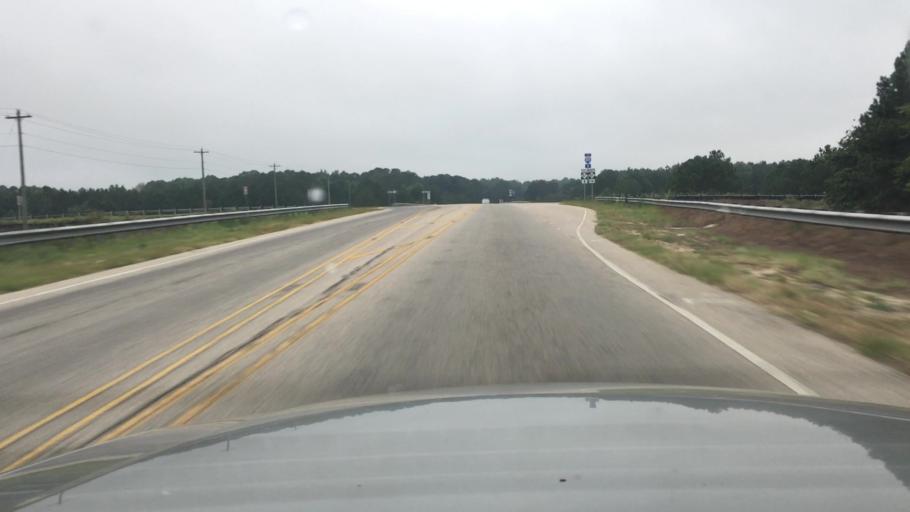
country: US
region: North Carolina
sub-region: Cumberland County
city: Fayetteville
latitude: 35.0102
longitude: -78.8663
